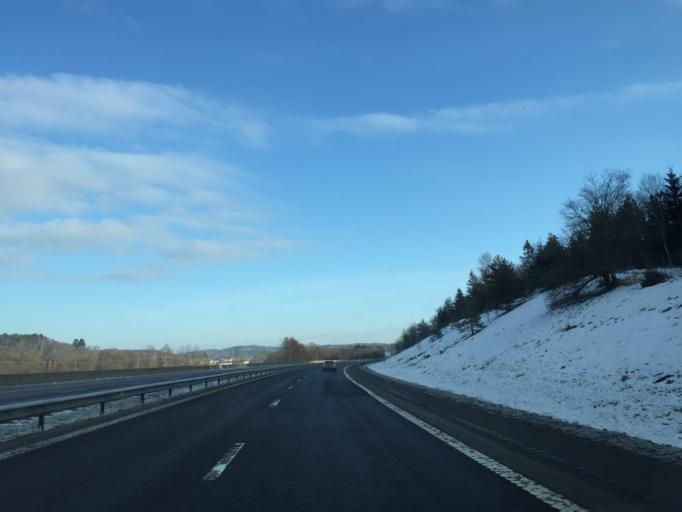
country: SE
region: Vaestra Goetaland
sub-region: Stenungsunds Kommun
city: Stora Hoga
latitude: 58.0429
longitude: 11.8489
